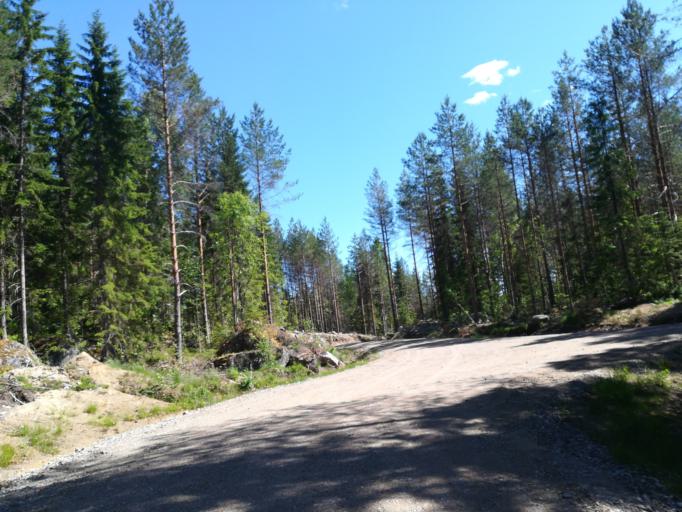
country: FI
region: Southern Savonia
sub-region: Mikkeli
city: Puumala
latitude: 61.6160
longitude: 28.1670
